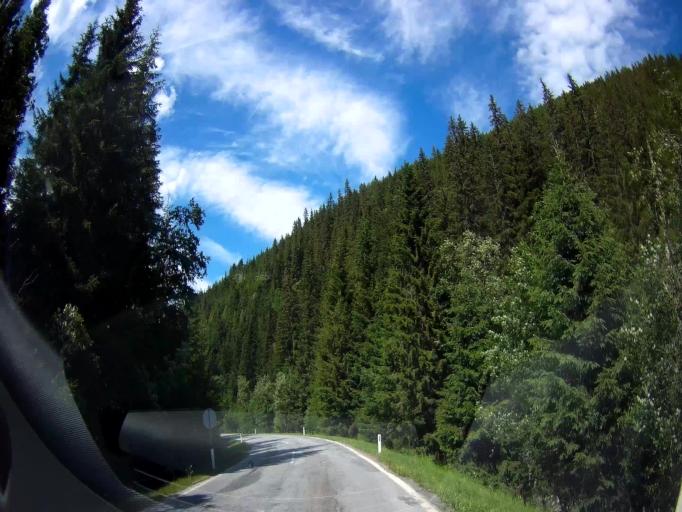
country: AT
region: Styria
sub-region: Politischer Bezirk Murau
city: Stadl an der Mur
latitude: 47.0115
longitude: 14.0095
